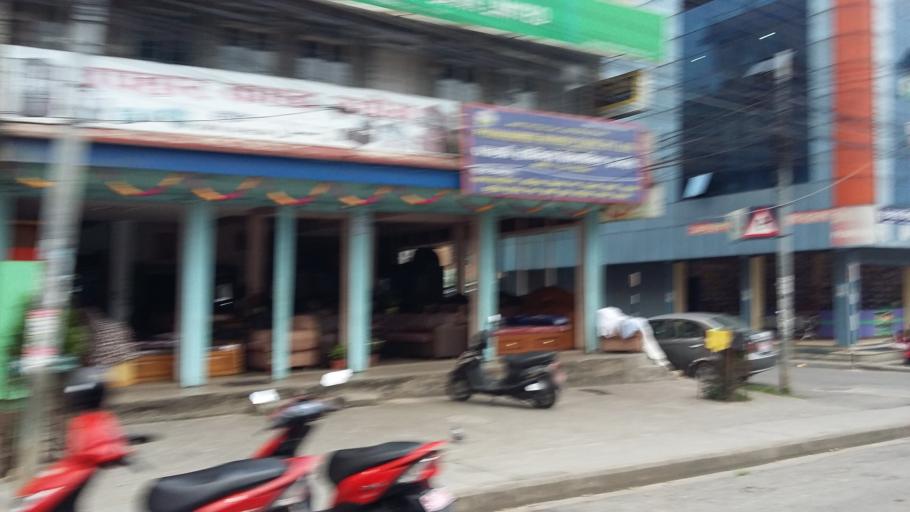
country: NP
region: Western Region
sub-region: Gandaki Zone
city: Pokhara
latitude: 28.2183
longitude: 83.9866
